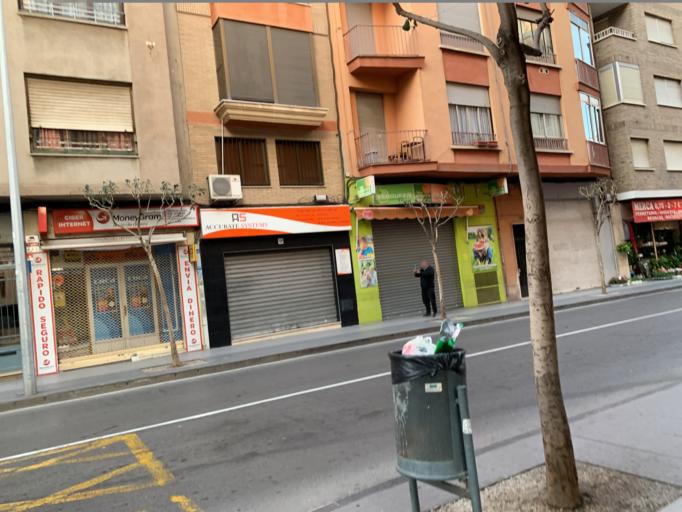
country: ES
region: Valencia
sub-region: Provincia de Castello
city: Castello de la Plana
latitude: 39.9895
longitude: -0.0395
